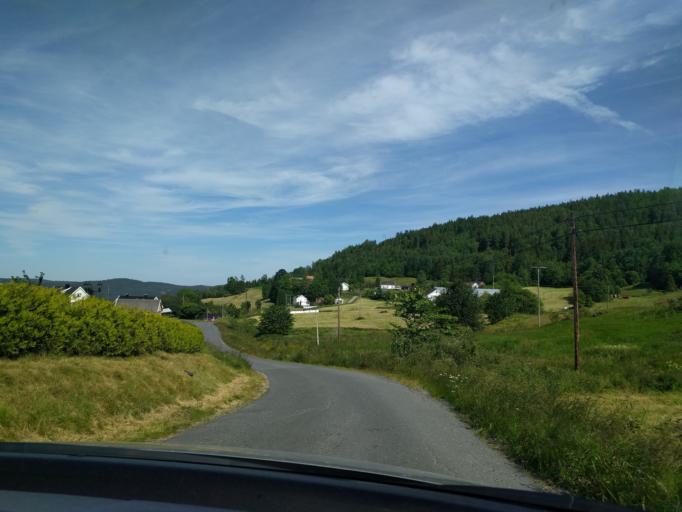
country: NO
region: Aust-Agder
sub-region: Gjerstad
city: Gjerstad
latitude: 58.8867
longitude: 8.9545
